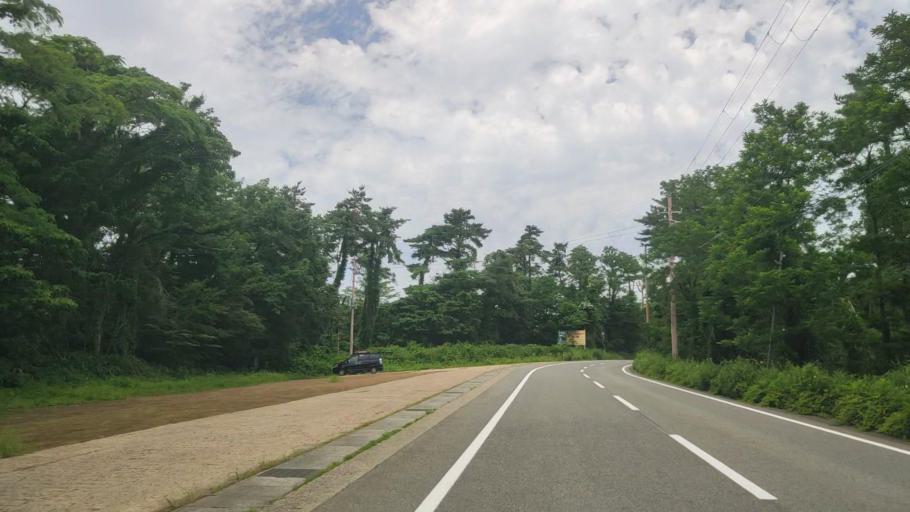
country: JP
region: Hyogo
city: Toyooka
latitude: 35.4987
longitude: 134.6822
